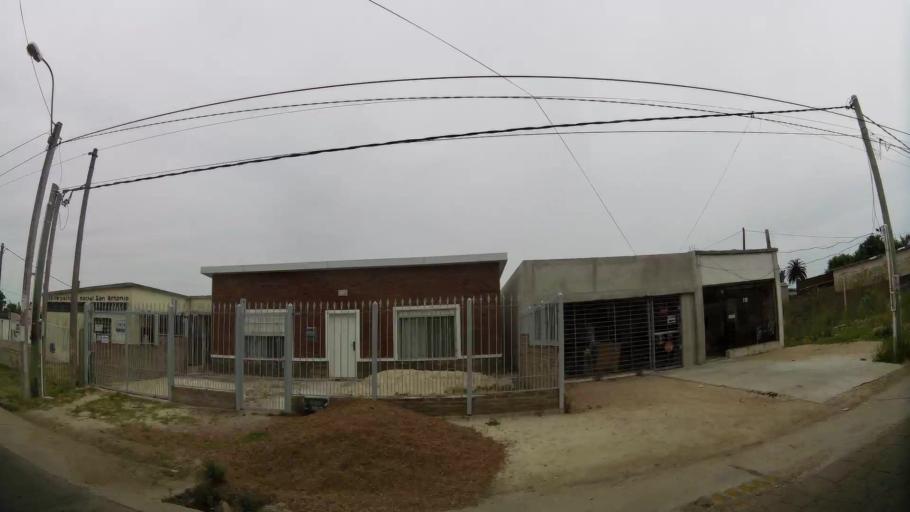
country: UY
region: Canelones
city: Las Piedras
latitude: -34.7328
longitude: -56.2277
